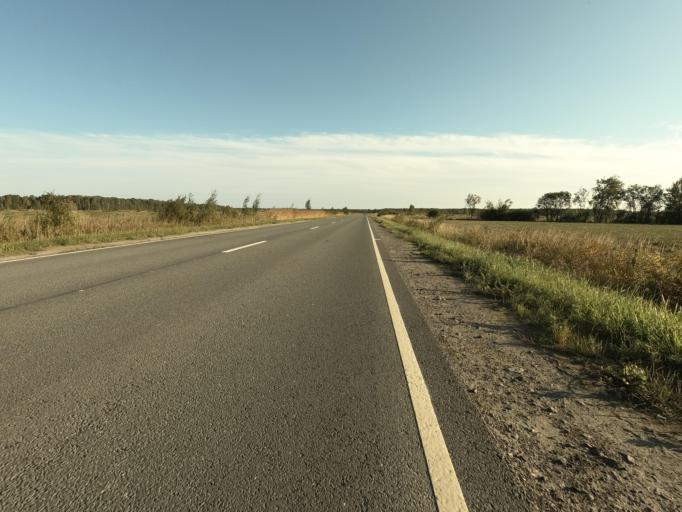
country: RU
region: St.-Petersburg
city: Sapernyy
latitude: 59.7384
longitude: 30.6528
